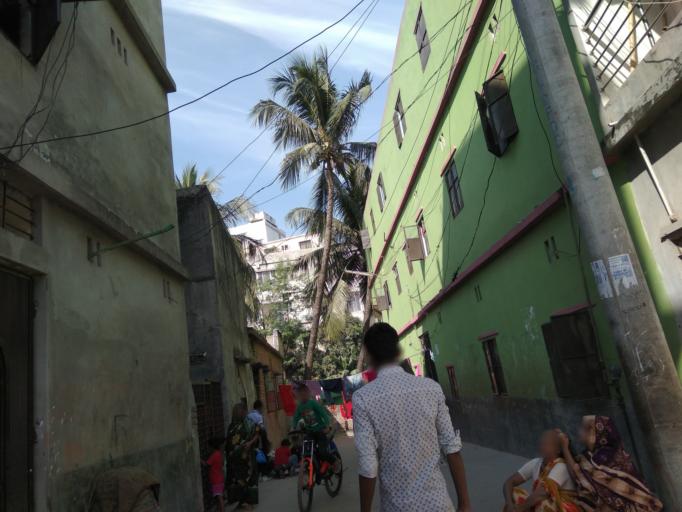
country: BD
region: Dhaka
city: Azimpur
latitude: 23.7764
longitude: 90.3583
